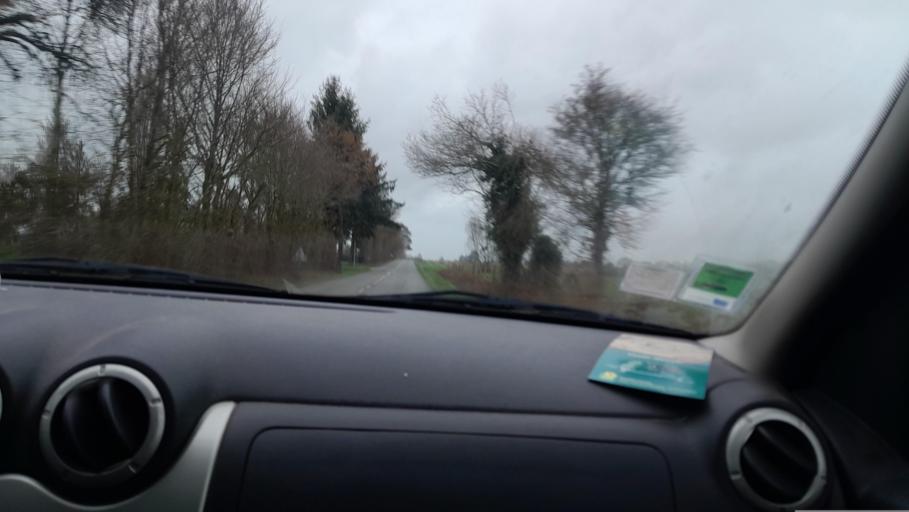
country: FR
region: Pays de la Loire
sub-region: Departement de la Mayenne
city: Ballots
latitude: 47.9343
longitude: -1.0888
